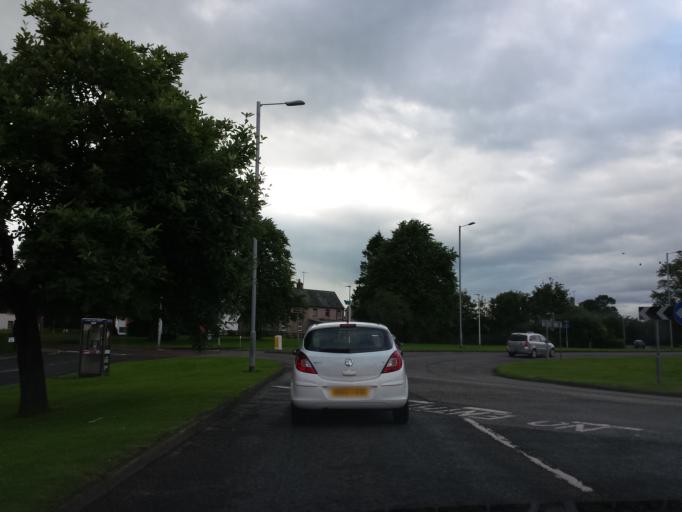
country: GB
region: Scotland
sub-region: Dumfries and Galloway
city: Dumfries
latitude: 55.0730
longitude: -3.6220
